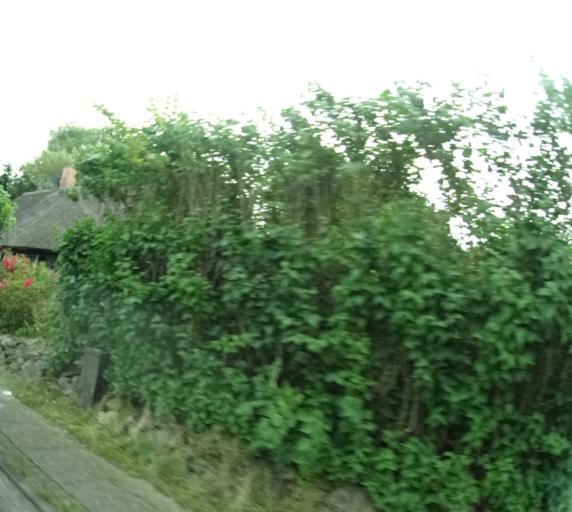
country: DK
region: Central Jutland
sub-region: Syddjurs Kommune
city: Ryomgard
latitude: 56.3856
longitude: 10.4756
